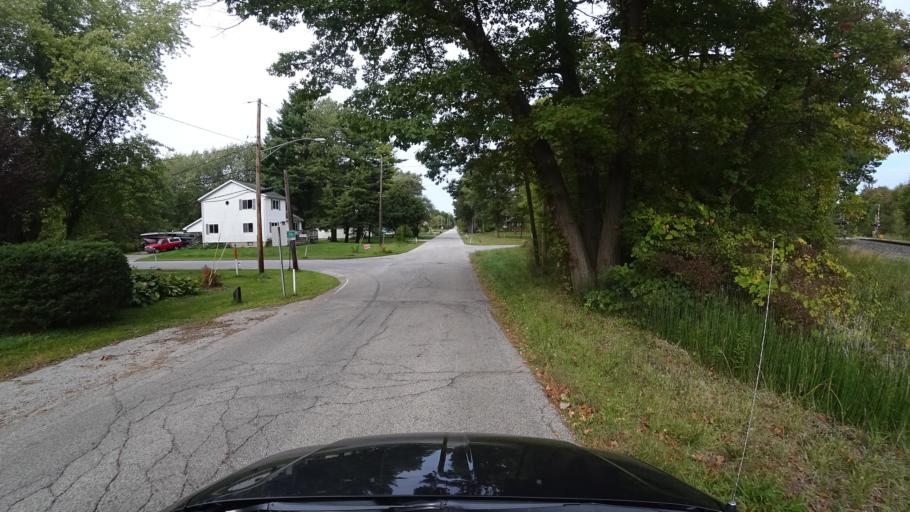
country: US
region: Indiana
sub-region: LaPorte County
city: Long Beach
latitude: 41.7377
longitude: -86.8162
